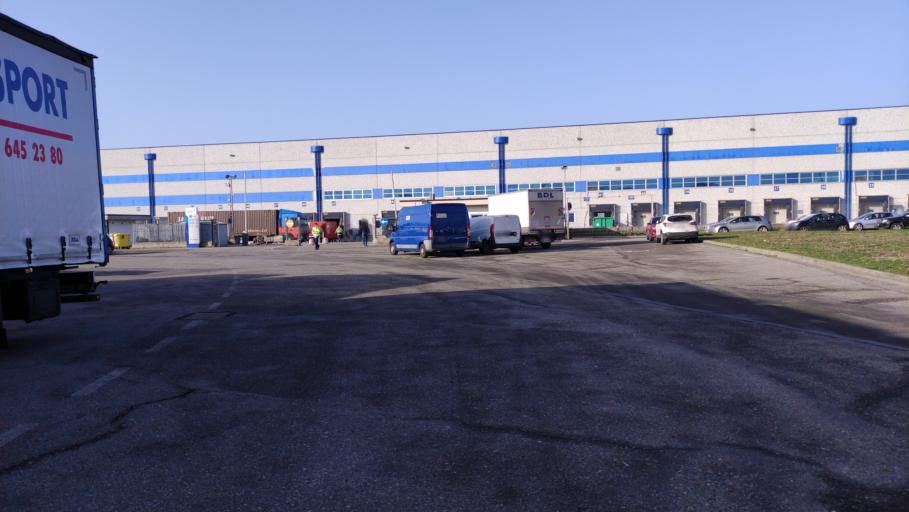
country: IT
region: Lombardy
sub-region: Provincia di Pavia
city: Landriano
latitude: 45.3015
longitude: 9.2708
